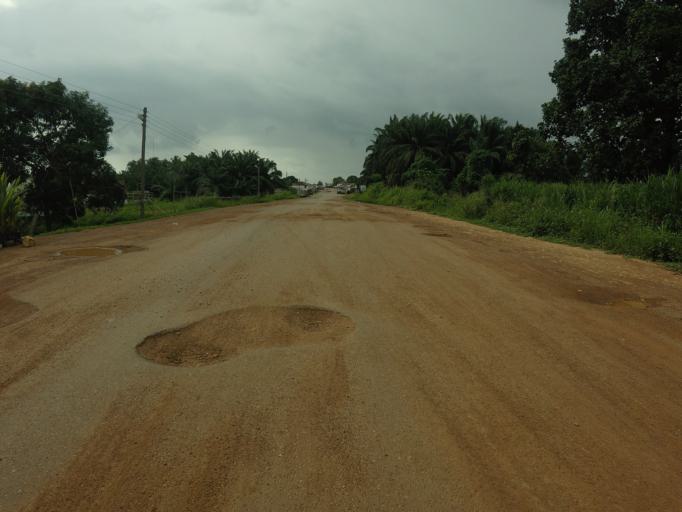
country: GH
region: Volta
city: Kpandu
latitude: 6.9947
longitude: 0.4392
